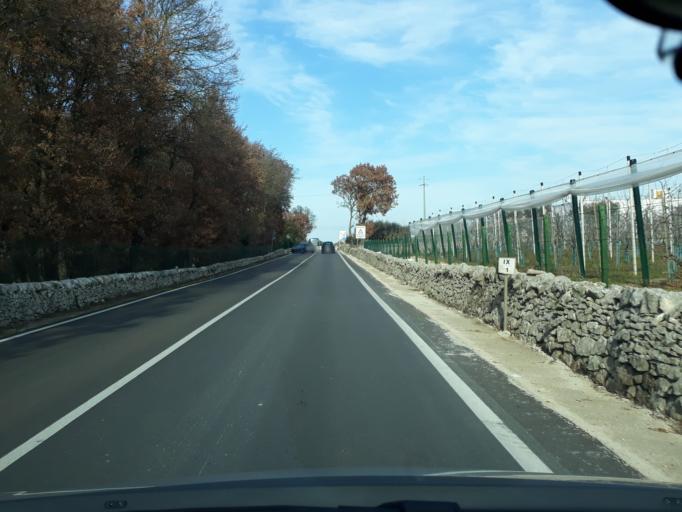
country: IT
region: Apulia
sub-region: Provincia di Bari
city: Locorotondo
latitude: 40.7715
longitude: 17.3344
